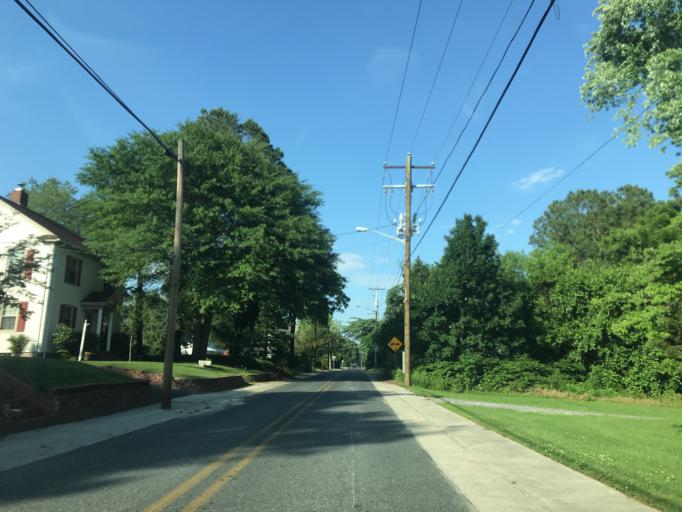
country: US
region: Maryland
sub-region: Wicomico County
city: Hebron
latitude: 38.5377
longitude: -75.7197
